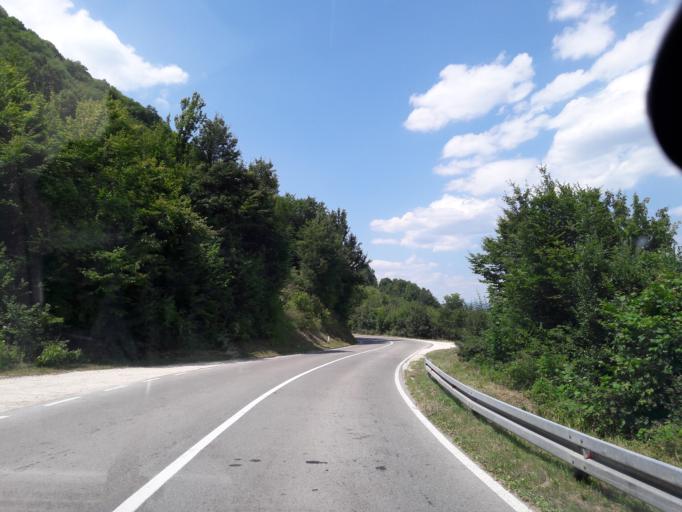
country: BA
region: Republika Srpska
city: Sipovo
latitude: 44.2055
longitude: 17.1371
